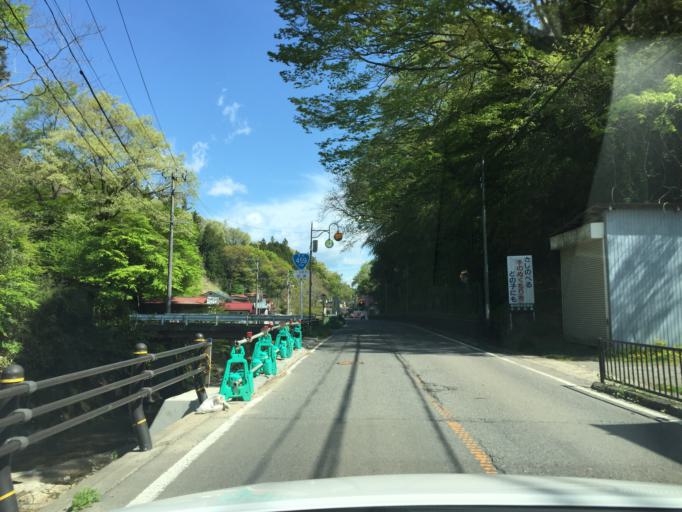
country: JP
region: Fukushima
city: Nihommatsu
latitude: 37.5631
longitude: 140.5081
